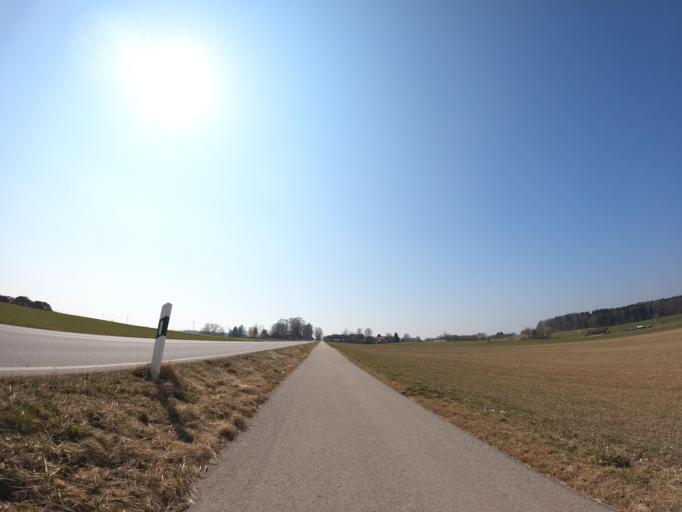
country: DE
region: Bavaria
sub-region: Upper Bavaria
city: Schaftlarn
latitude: 48.0168
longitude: 11.4118
